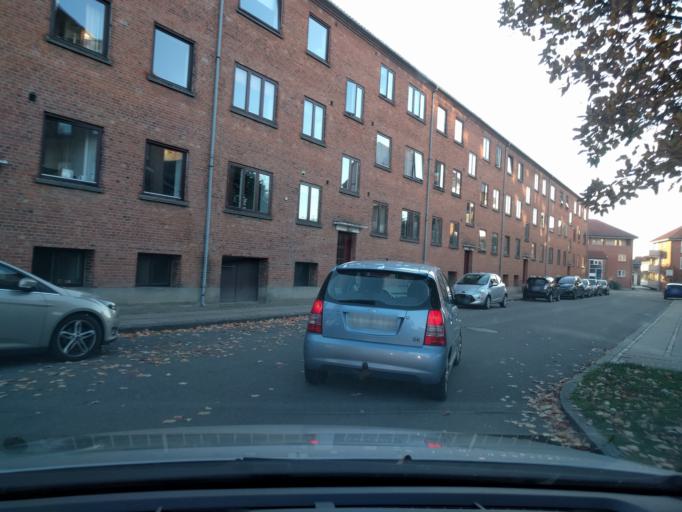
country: DK
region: Zealand
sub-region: Guldborgsund Kommune
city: Nykobing Falster
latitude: 54.7723
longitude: 11.8686
